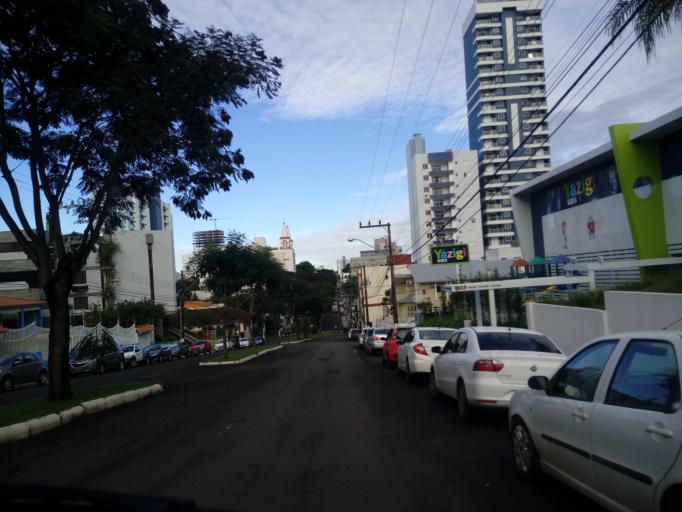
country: BR
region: Santa Catarina
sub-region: Chapeco
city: Chapeco
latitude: -27.1037
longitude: -52.6097
